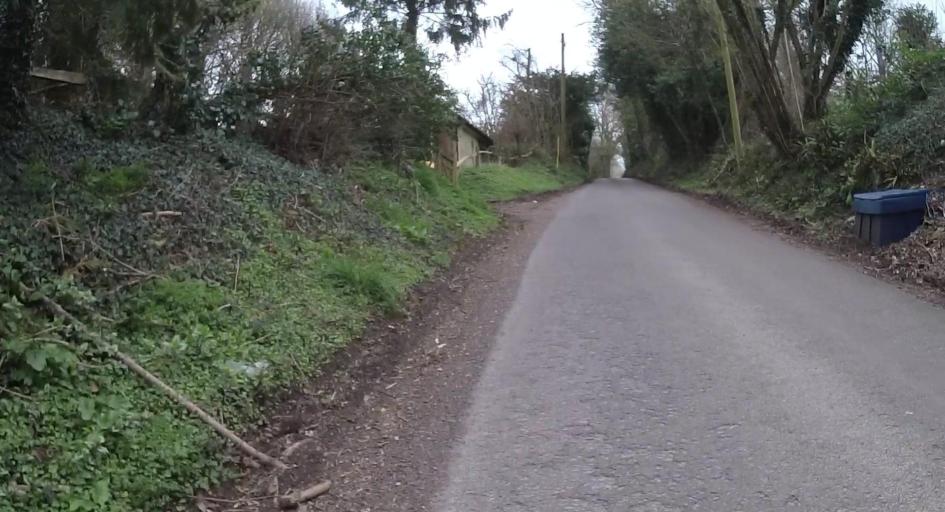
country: GB
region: England
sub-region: Hampshire
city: Four Marks
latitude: 51.0908
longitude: -1.0594
